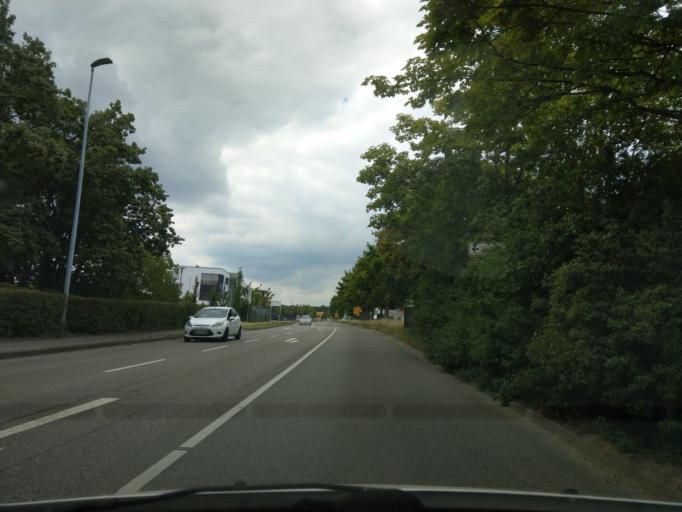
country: DE
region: Baden-Wuerttemberg
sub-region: Regierungsbezirk Stuttgart
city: Ostfildern
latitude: 48.7065
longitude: 9.2534
